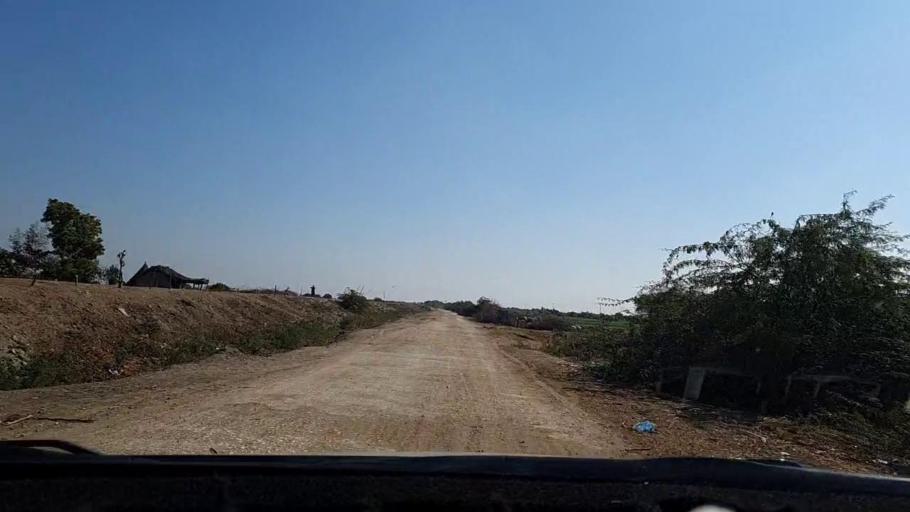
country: PK
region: Sindh
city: Tando Mittha Khan
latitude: 25.7715
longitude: 69.2940
